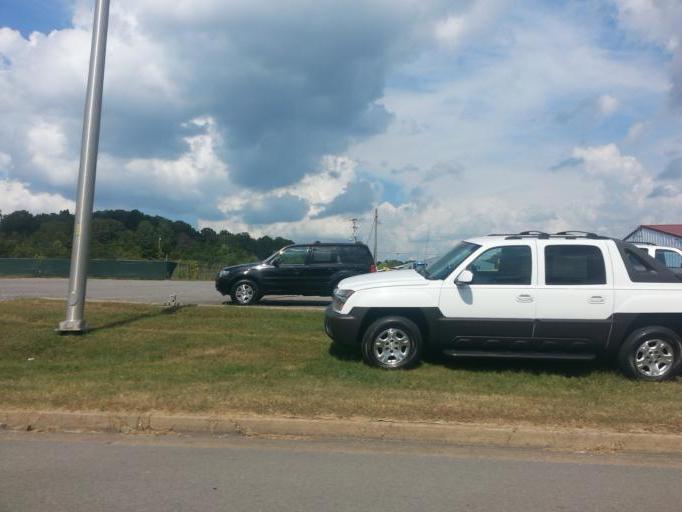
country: US
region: Tennessee
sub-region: Dickson County
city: Dickson
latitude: 36.0570
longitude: -87.3712
